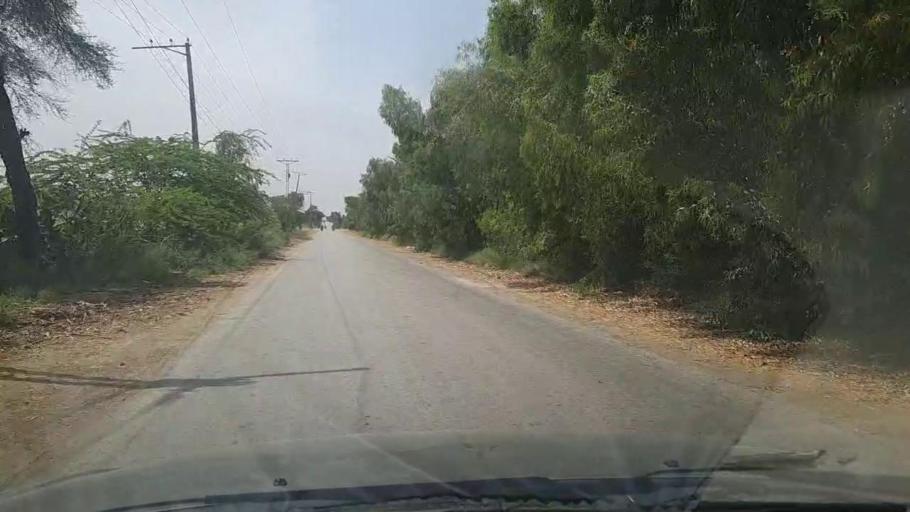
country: PK
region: Sindh
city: Bhiria
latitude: 26.9031
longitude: 68.2061
